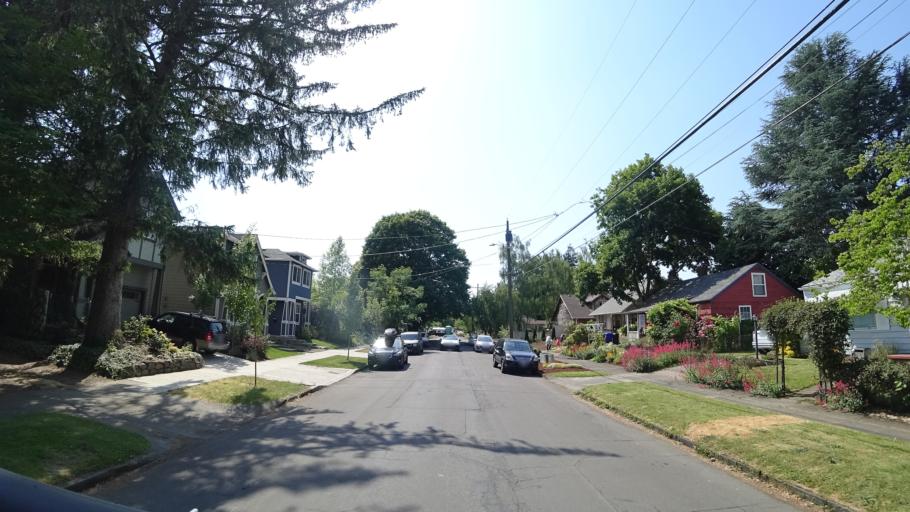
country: US
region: Oregon
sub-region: Multnomah County
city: Lents
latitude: 45.5161
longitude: -122.5706
